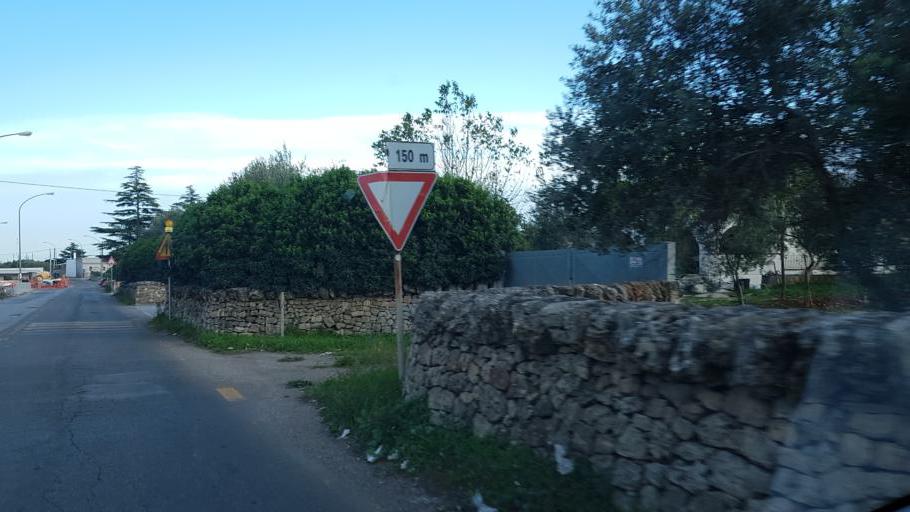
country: IT
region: Apulia
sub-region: Provincia di Taranto
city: Martina Franca
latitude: 40.7176
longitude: 17.3312
